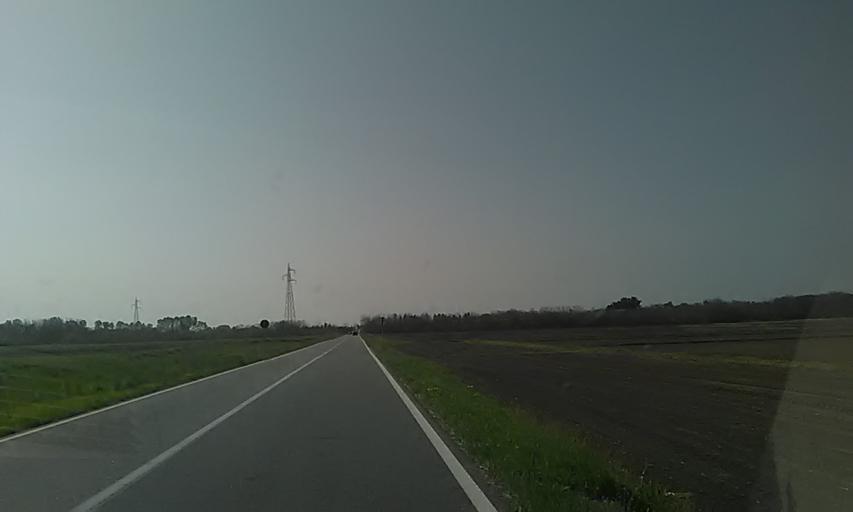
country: IT
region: Piedmont
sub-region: Provincia di Vercelli
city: Lenta
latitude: 45.5458
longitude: 8.3849
